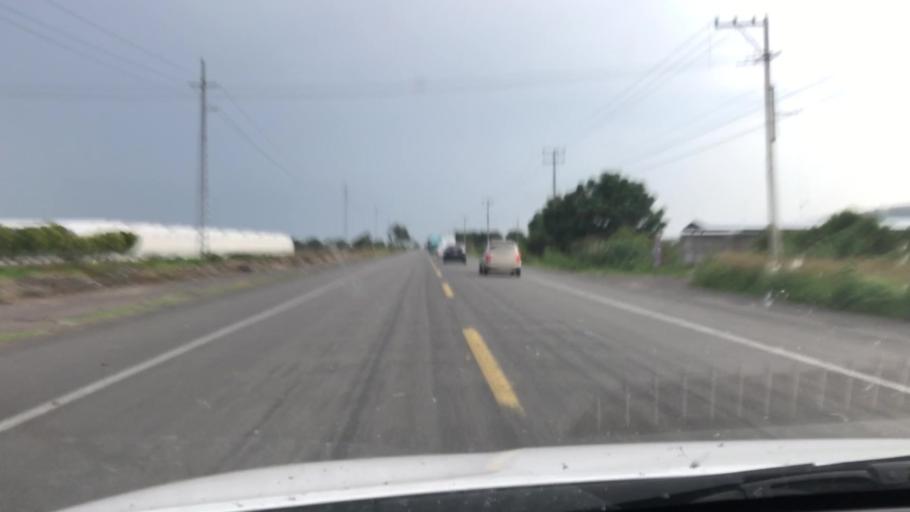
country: MX
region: Michoacan
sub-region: Vista Hermosa
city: Los Pilares
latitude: 20.2775
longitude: -102.3813
